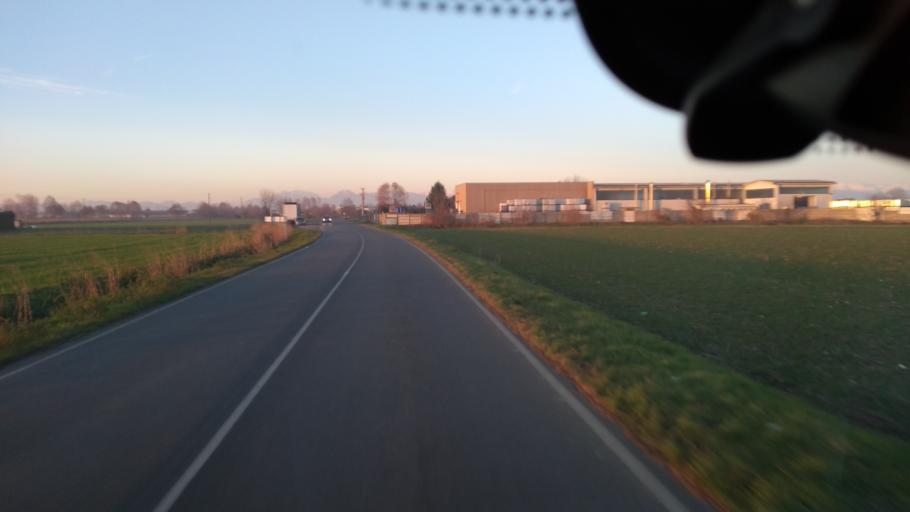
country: IT
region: Lombardy
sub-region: Provincia di Bergamo
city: Calvenzano
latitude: 45.4817
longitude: 9.6020
